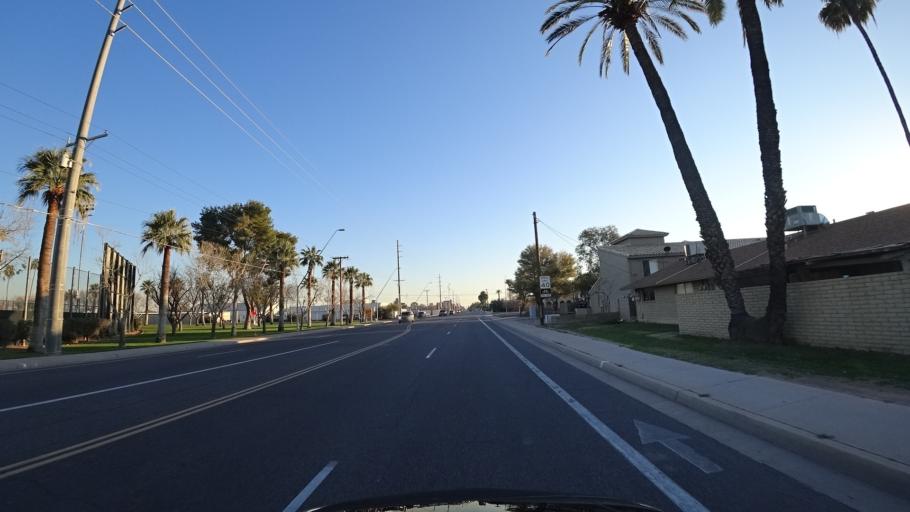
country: US
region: Arizona
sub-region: Maricopa County
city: Mesa
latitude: 33.4278
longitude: -111.8314
